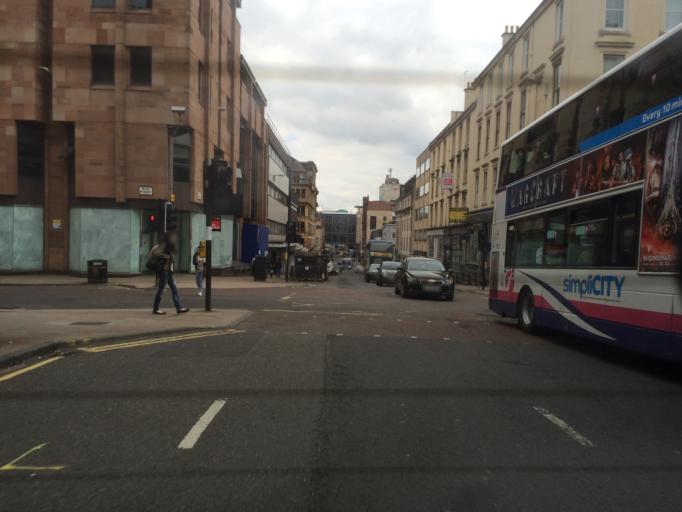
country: GB
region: Scotland
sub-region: Glasgow City
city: Glasgow
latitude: 55.8641
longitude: -4.2578
